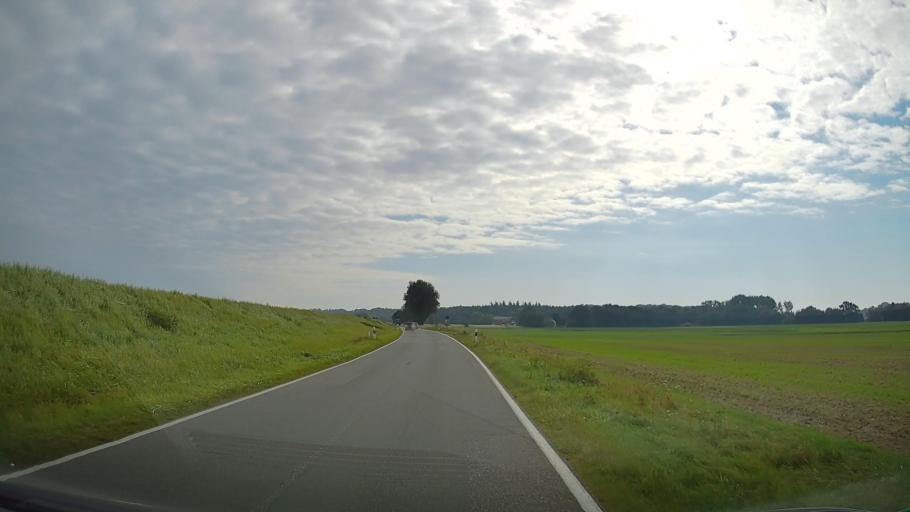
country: DE
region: Schleswig-Holstein
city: Blekendorf
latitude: 54.3311
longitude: 10.6492
